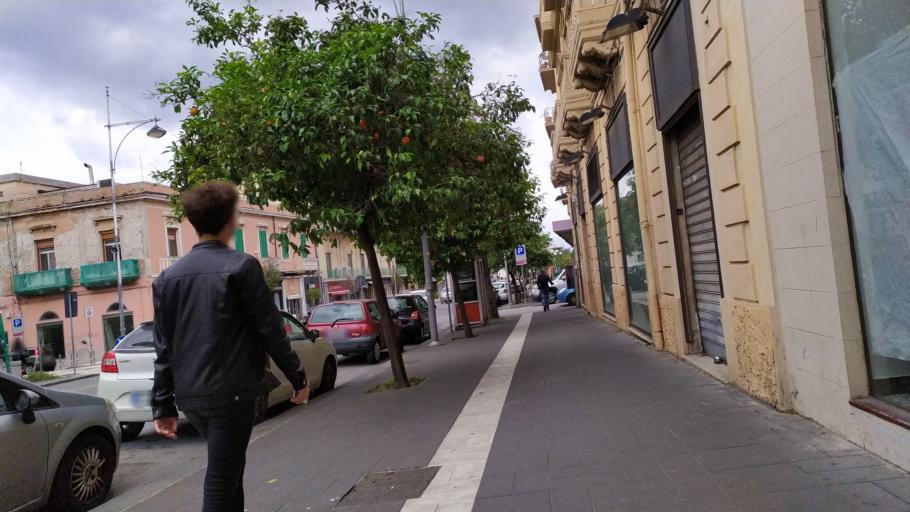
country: IT
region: Sicily
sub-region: Messina
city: Messina
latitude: 38.1874
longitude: 15.5549
